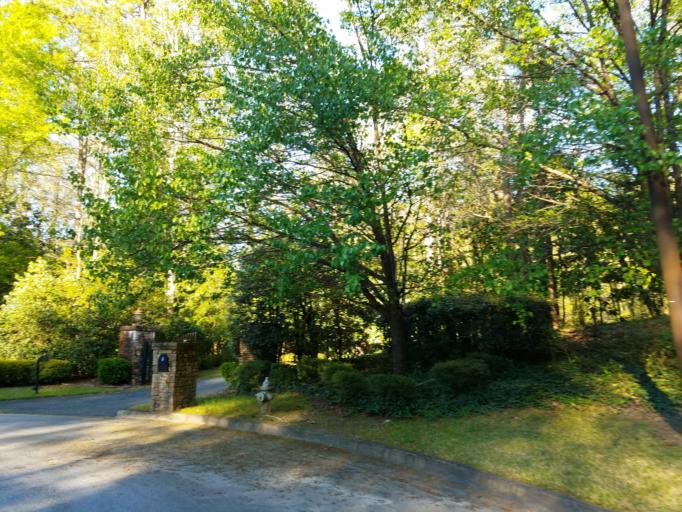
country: US
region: Georgia
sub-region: Cobb County
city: Vinings
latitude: 33.8496
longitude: -84.4520
